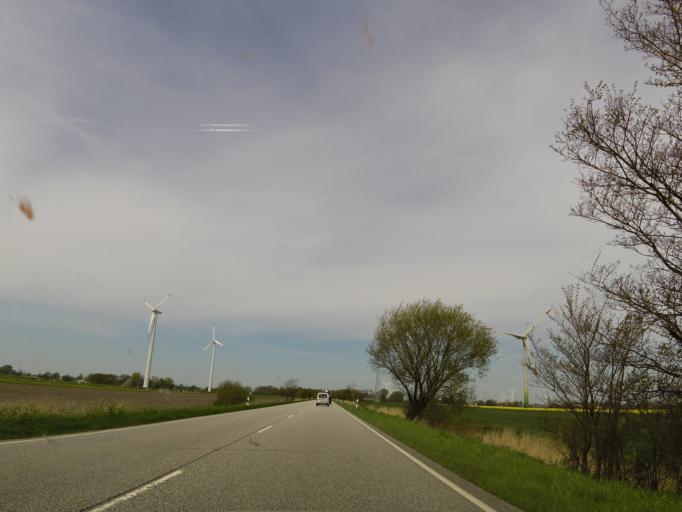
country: DE
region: Schleswig-Holstein
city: Hemme
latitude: 54.2691
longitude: 9.0209
